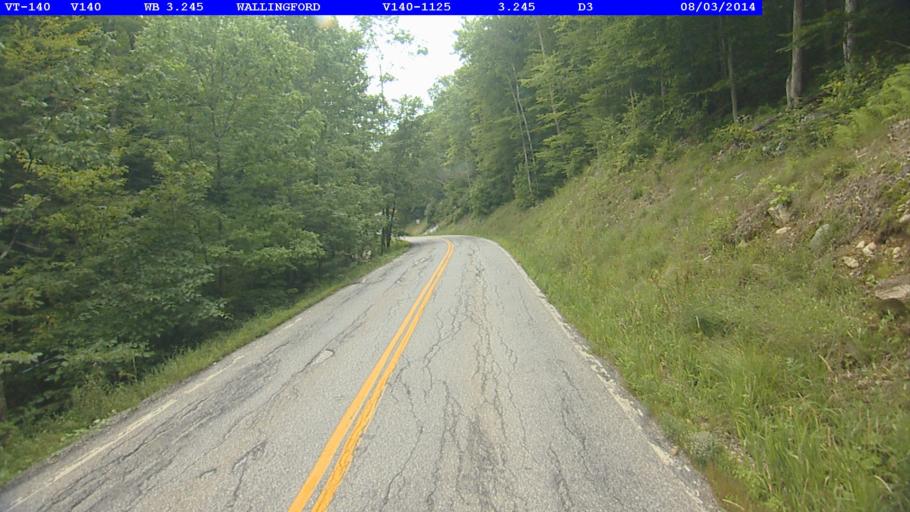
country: US
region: Vermont
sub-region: Rutland County
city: Rutland
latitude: 43.4598
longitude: -72.9240
